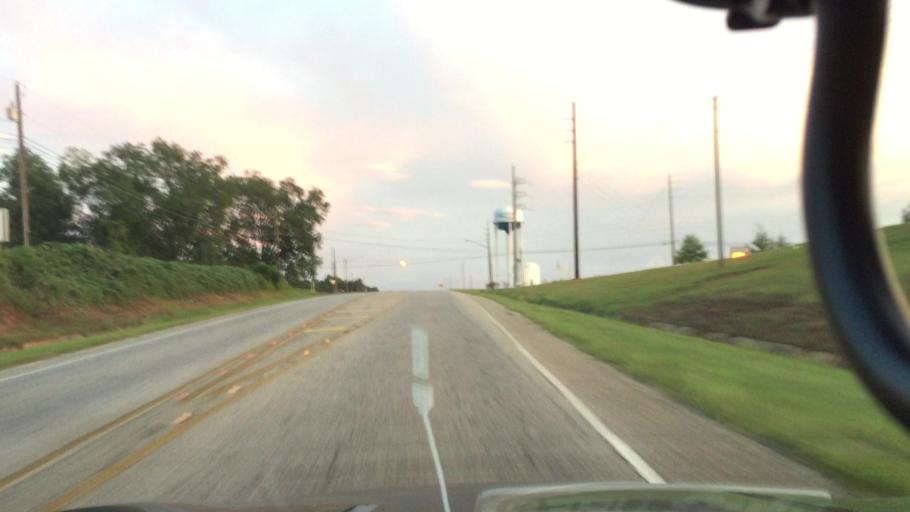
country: US
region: Alabama
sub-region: Coffee County
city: Enterprise
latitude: 31.3621
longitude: -85.8675
